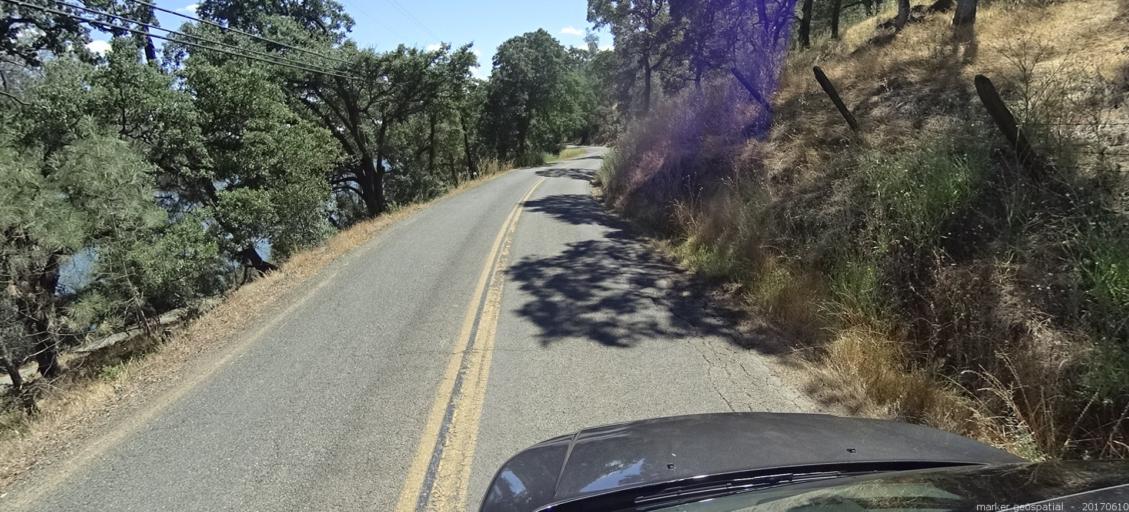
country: US
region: California
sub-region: Butte County
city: Oroville
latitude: 39.5442
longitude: -121.5451
